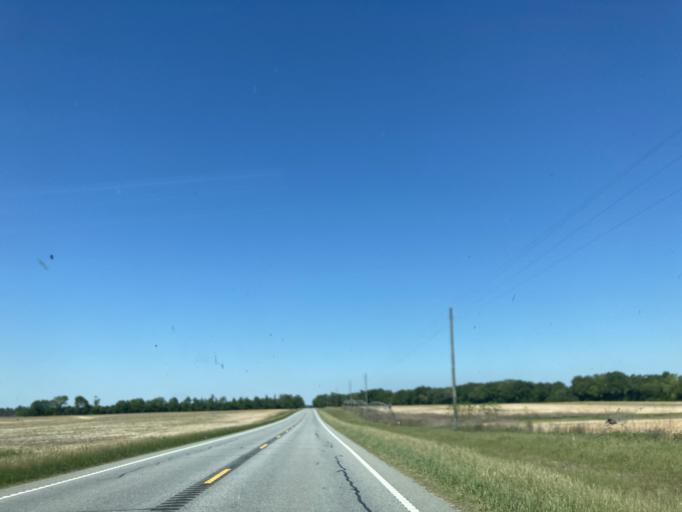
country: US
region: Georgia
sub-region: Baker County
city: Newton
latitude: 31.2214
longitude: -84.4480
